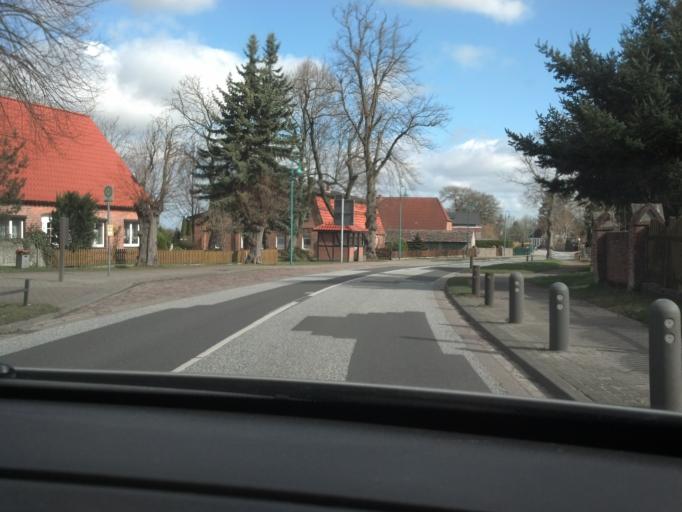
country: DE
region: Schleswig-Holstein
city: Gudow
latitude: 53.4936
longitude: 10.8334
